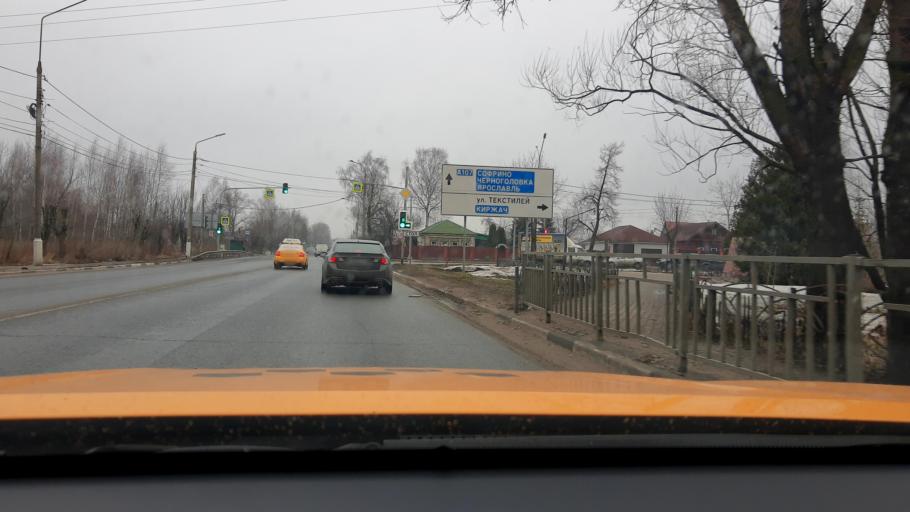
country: RU
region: Moskovskaya
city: Noginsk
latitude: 55.8796
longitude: 38.4292
